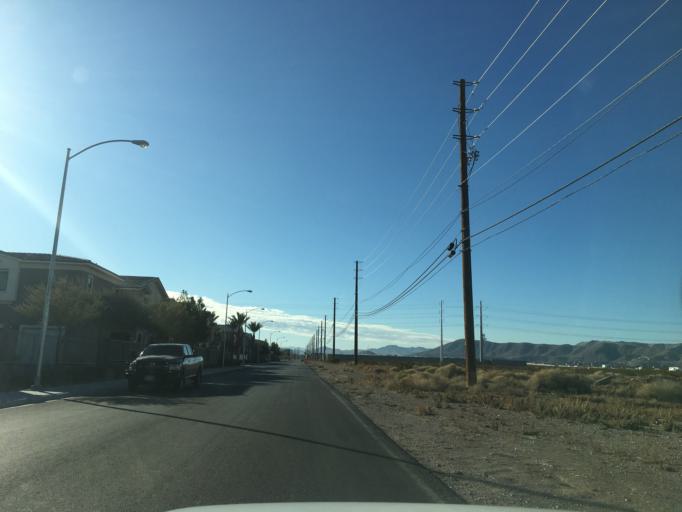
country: US
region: Nevada
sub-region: Clark County
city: Enterprise
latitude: 36.0058
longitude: -115.1703
